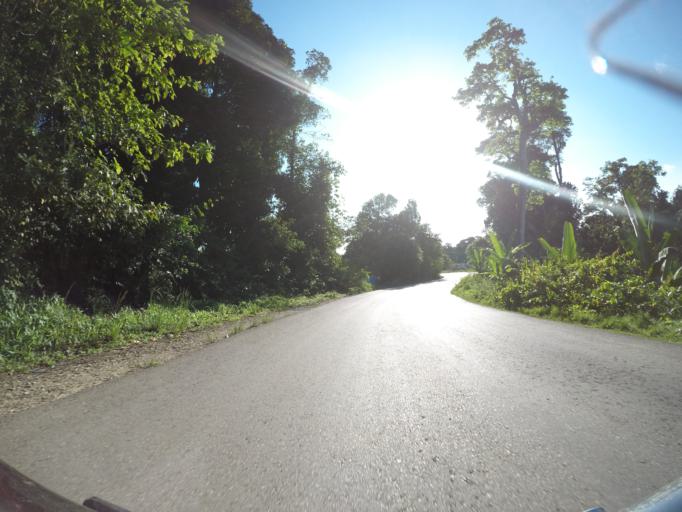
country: TZ
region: Pemba South
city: Mtambile
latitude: -5.3263
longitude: 39.7370
